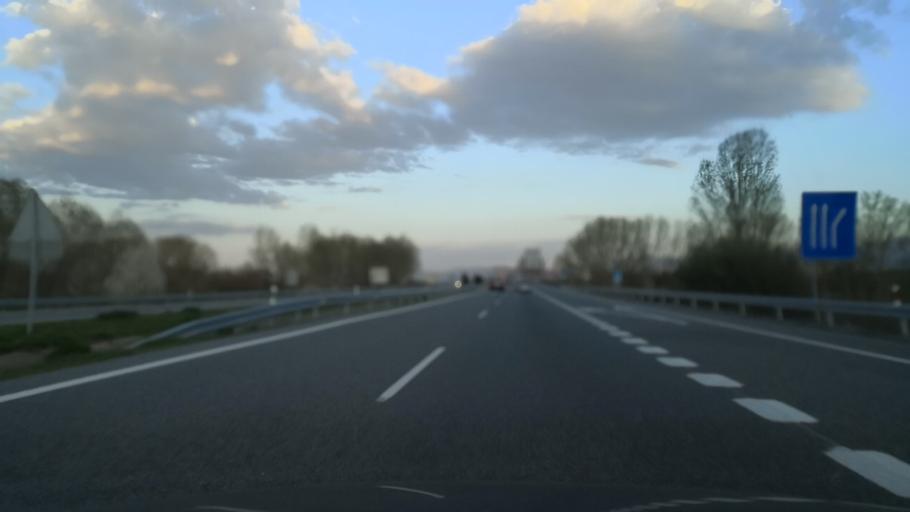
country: ES
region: Castille and Leon
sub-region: Provincia de Leon
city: Carracedelo
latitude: 42.5677
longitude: -6.7333
